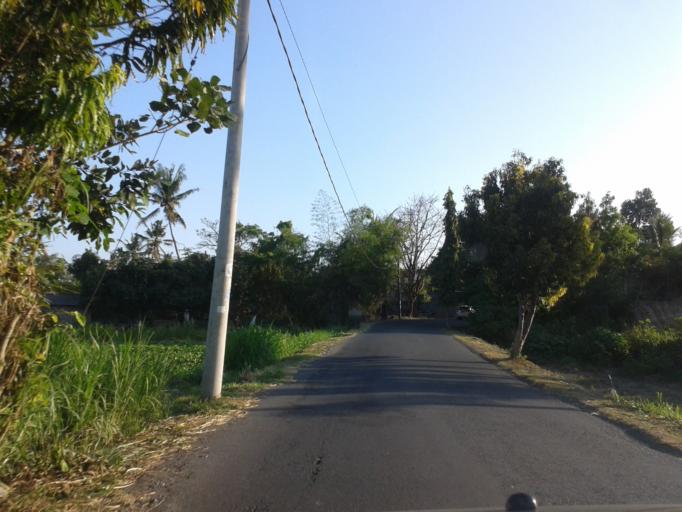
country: ID
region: Bali
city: Semarapura
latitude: -8.5632
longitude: 115.3865
